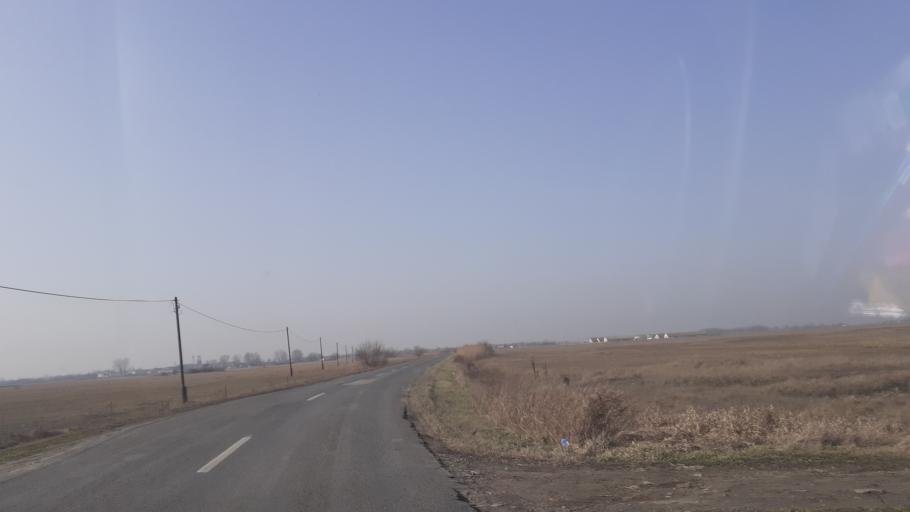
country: HU
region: Bacs-Kiskun
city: Kunszentmiklos
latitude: 47.0234
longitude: 19.1642
